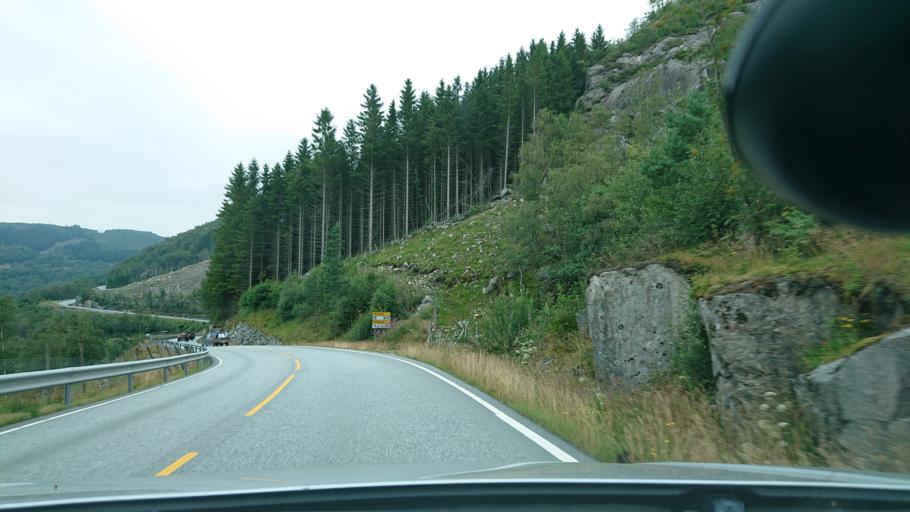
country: NO
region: Rogaland
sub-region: Hjelmeland
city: Hjelmelandsvagen
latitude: 59.1677
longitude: 6.1399
